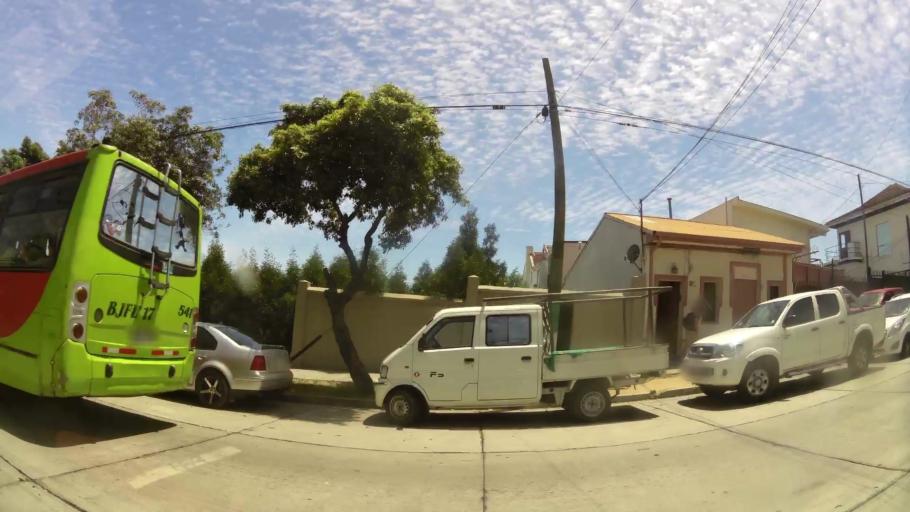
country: CL
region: Valparaiso
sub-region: Provincia de Valparaiso
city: Valparaiso
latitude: -33.0361
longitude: -71.5936
